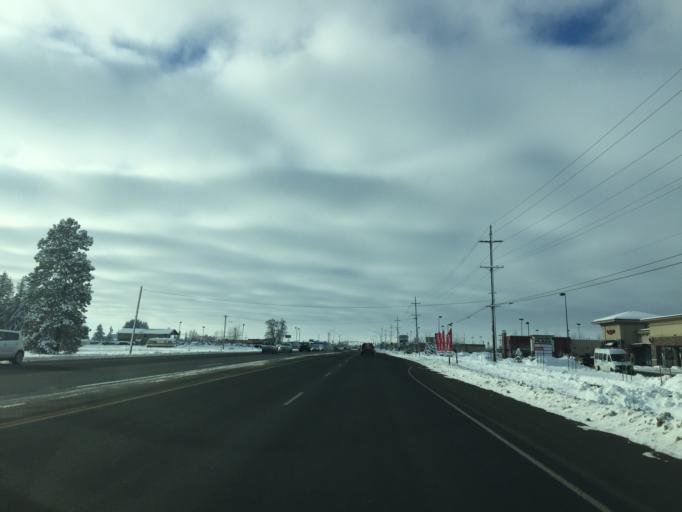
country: US
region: Washington
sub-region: Spokane County
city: Airway Heights
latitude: 47.6431
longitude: -117.5536
